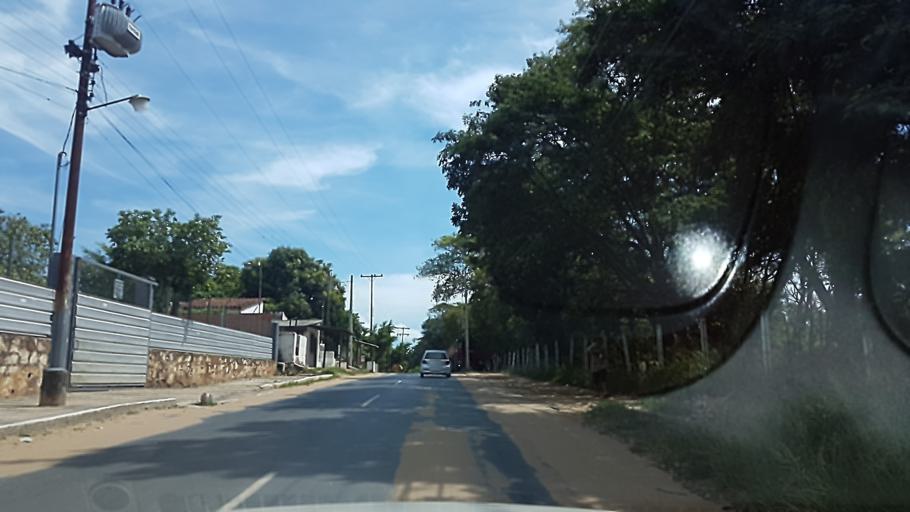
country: PY
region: Central
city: Colonia Mariano Roque Alonso
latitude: -25.1863
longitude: -57.5407
